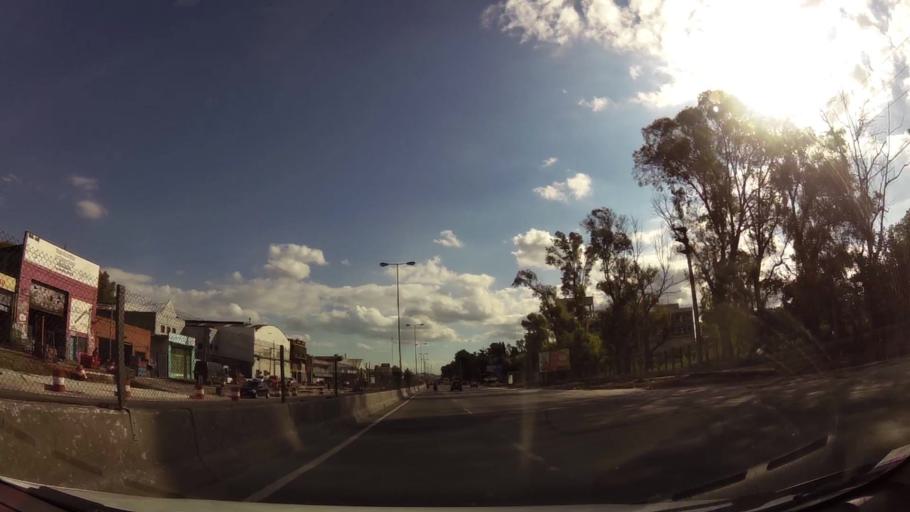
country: AR
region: Buenos Aires
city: San Justo
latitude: -34.6953
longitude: -58.5749
